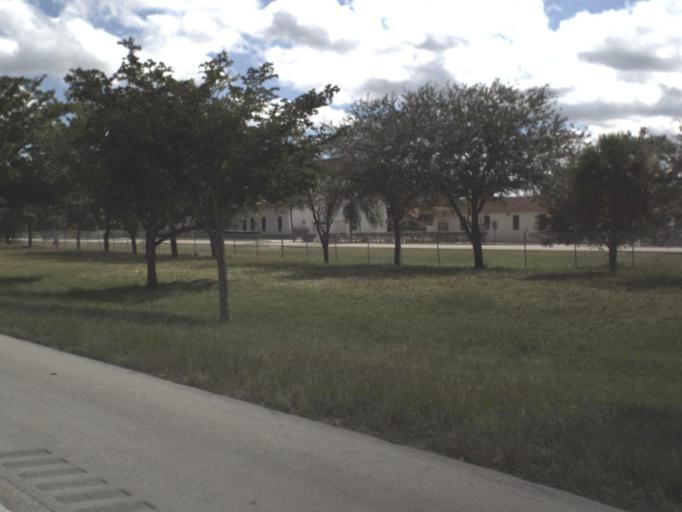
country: US
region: Florida
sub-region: Miami-Dade County
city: Lake Lucerne
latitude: 25.9719
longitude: -80.2582
